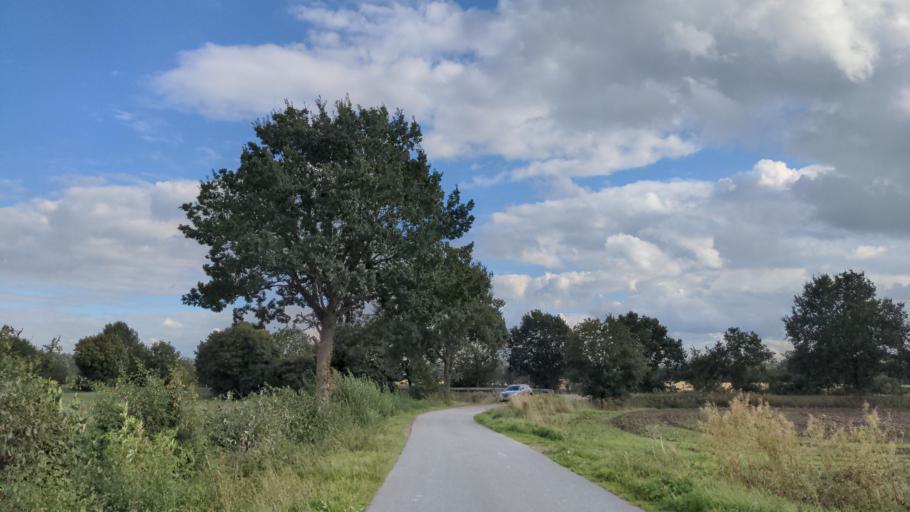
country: DE
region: Schleswig-Holstein
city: Monkhagen
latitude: 53.9342
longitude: 10.5858
